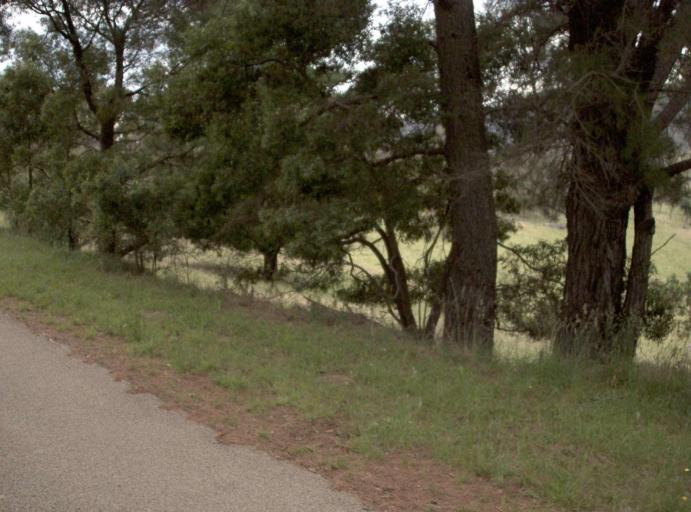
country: AU
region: Victoria
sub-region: East Gippsland
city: Bairnsdale
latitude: -37.5741
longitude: 147.1861
